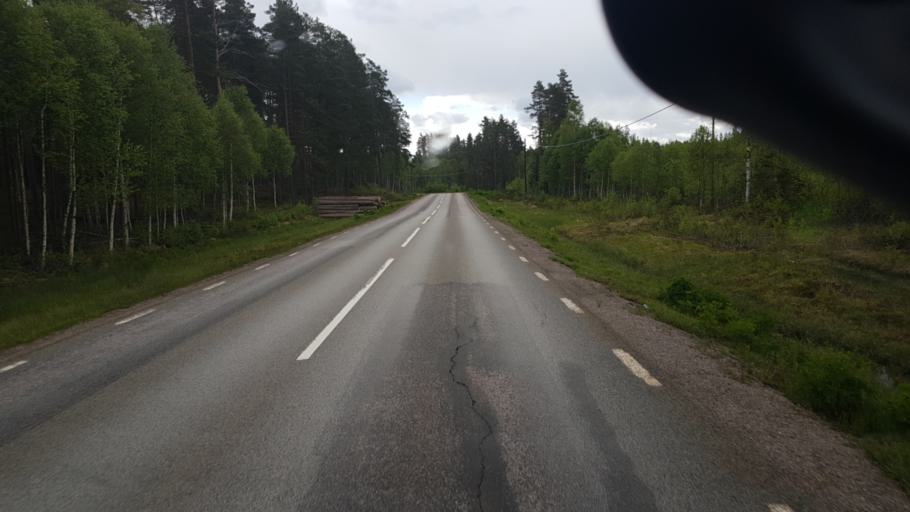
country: SE
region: Vaermland
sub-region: Arjangs Kommun
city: Arjaeng
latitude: 59.5547
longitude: 12.1655
